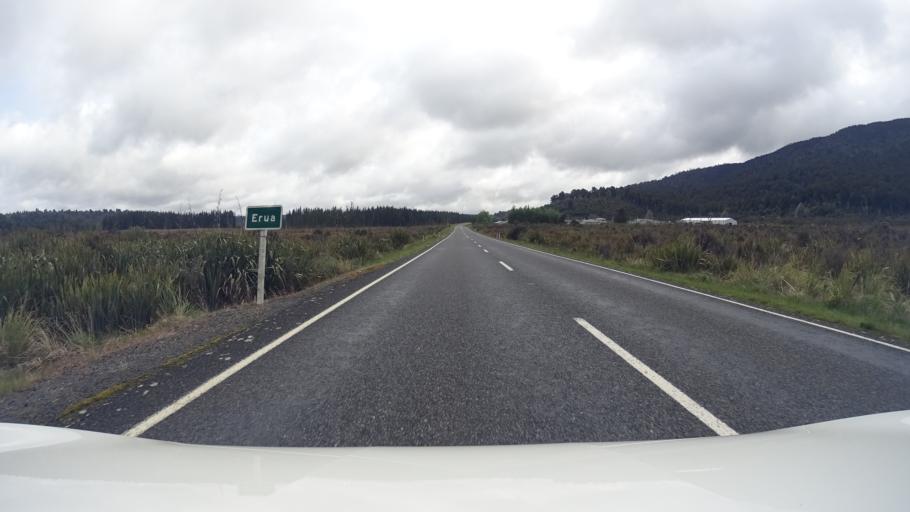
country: NZ
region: Manawatu-Wanganui
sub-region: Ruapehu District
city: Waiouru
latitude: -39.2300
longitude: 175.3947
